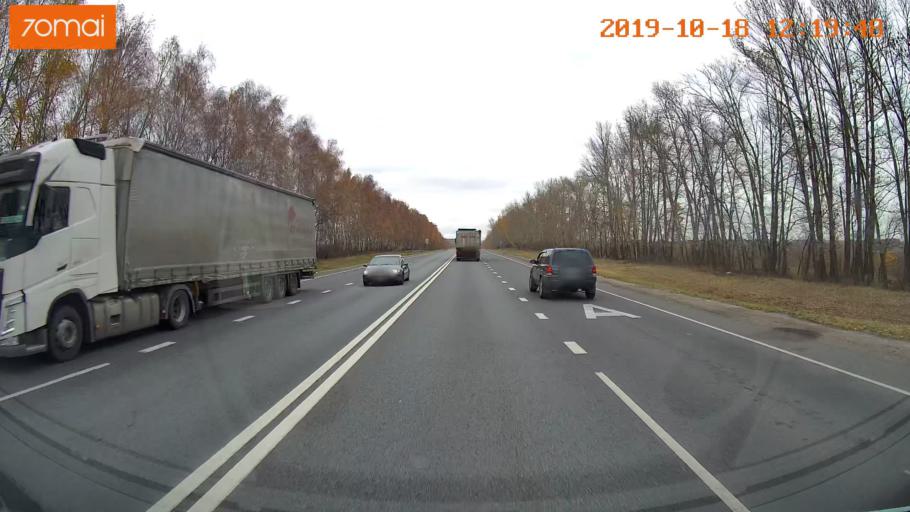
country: RU
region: Rjazan
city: Zakharovo
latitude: 54.4882
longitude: 39.4727
